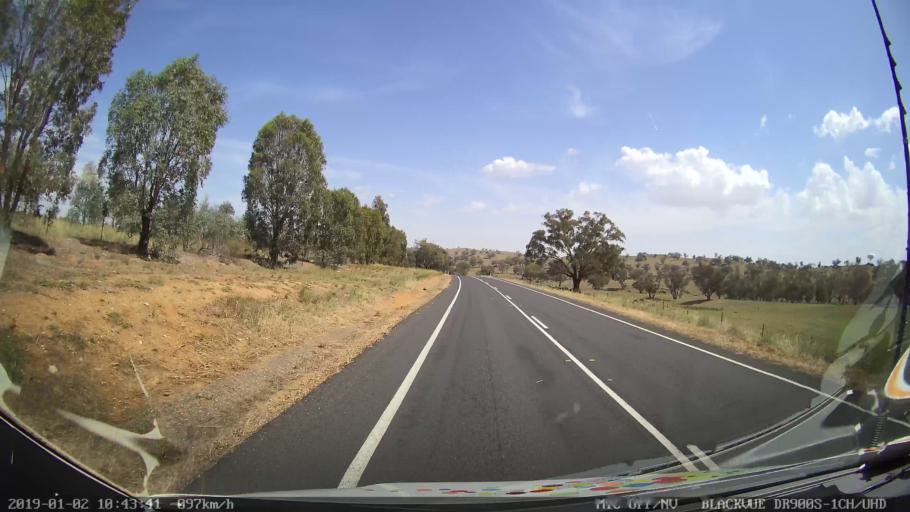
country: AU
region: New South Wales
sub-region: Cootamundra
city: Cootamundra
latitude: -34.7693
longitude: 148.3024
